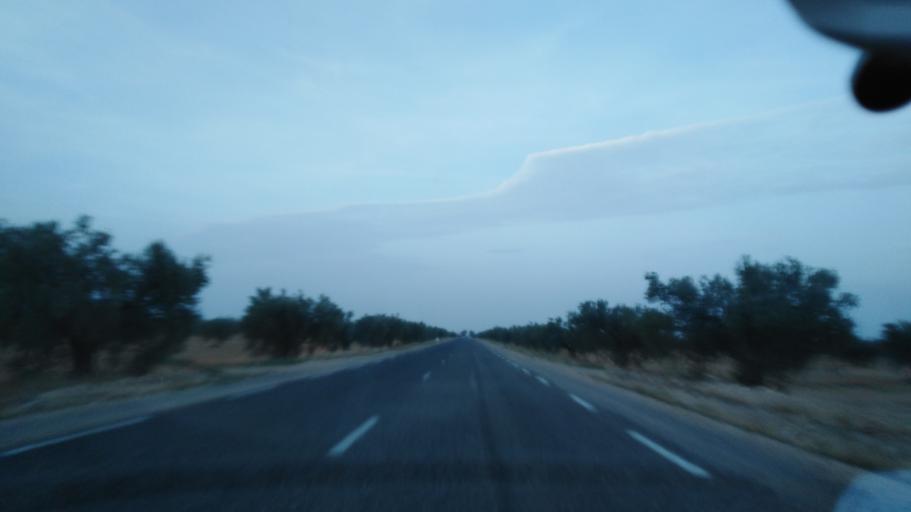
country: TN
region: Al Mahdiyah
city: Shurban
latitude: 34.9364
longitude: 10.3931
